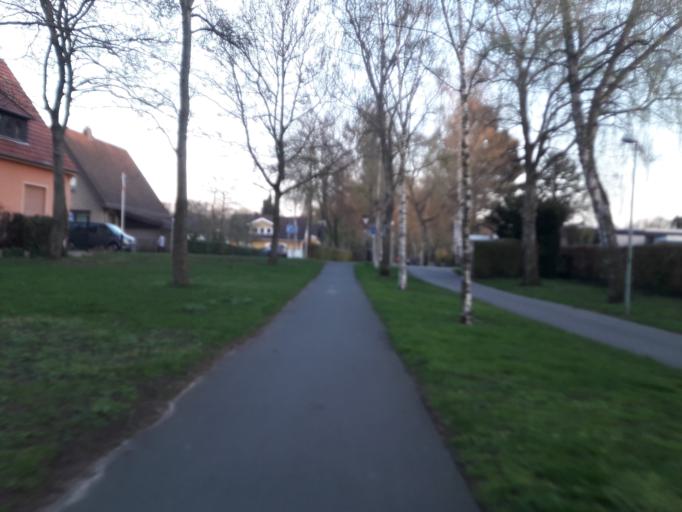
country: DE
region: North Rhine-Westphalia
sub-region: Regierungsbezirk Detmold
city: Paderborn
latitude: 51.7267
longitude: 8.7473
